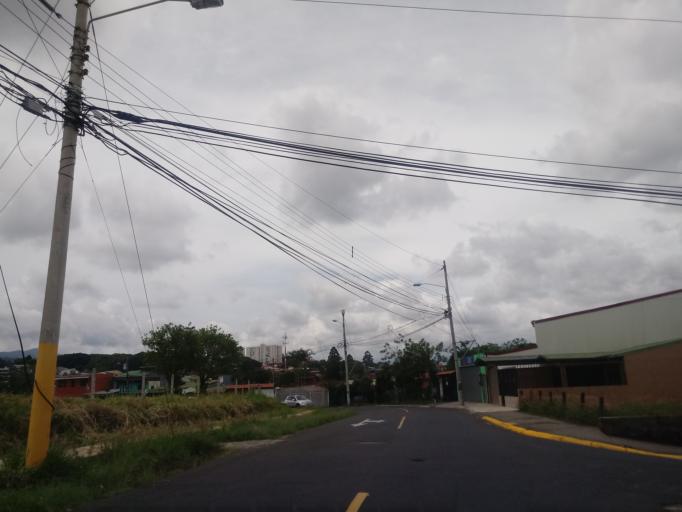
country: CR
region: Heredia
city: Heredia
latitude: 10.0054
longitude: -84.1153
